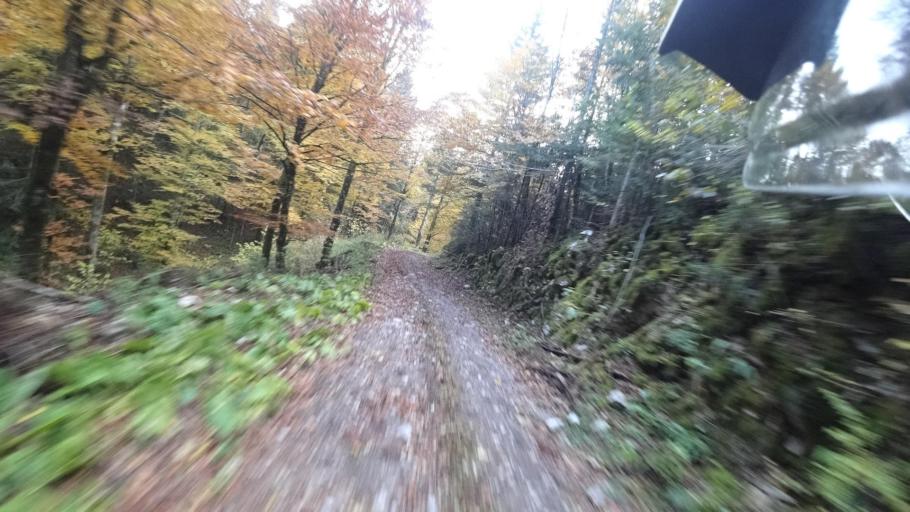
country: HR
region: Primorsko-Goranska
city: Vrbovsko
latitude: 45.2155
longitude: 15.0678
